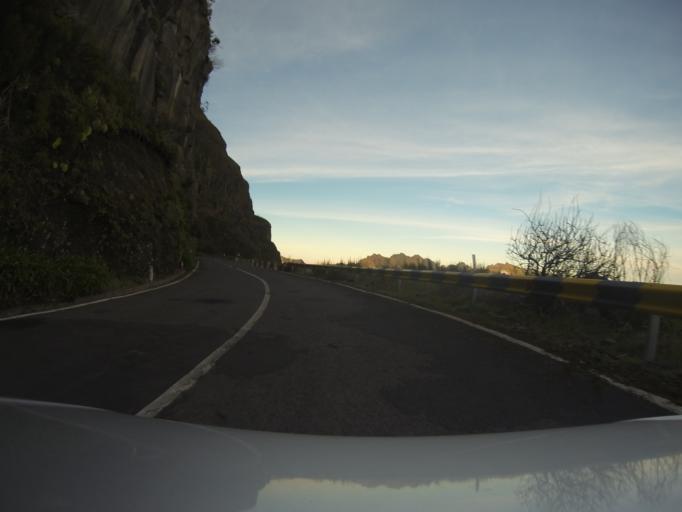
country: PT
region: Madeira
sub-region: Sao Vicente
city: Sao Vicente
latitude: 32.7417
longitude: -17.0475
